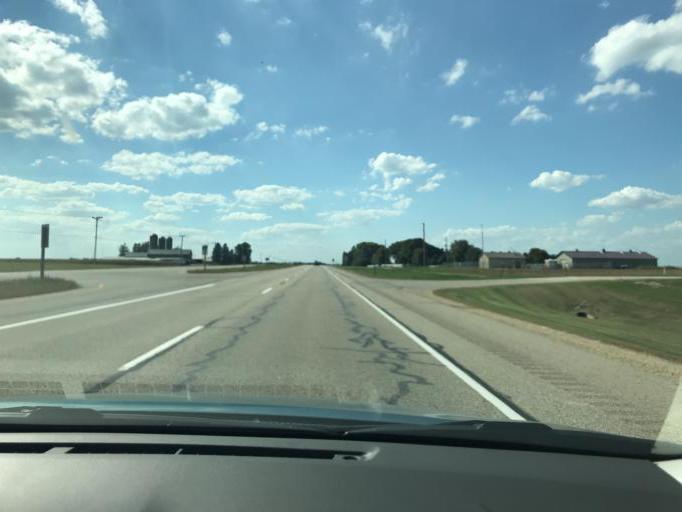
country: US
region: Wisconsin
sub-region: Kenosha County
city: Powers Lake
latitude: 42.5817
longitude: -88.3147
